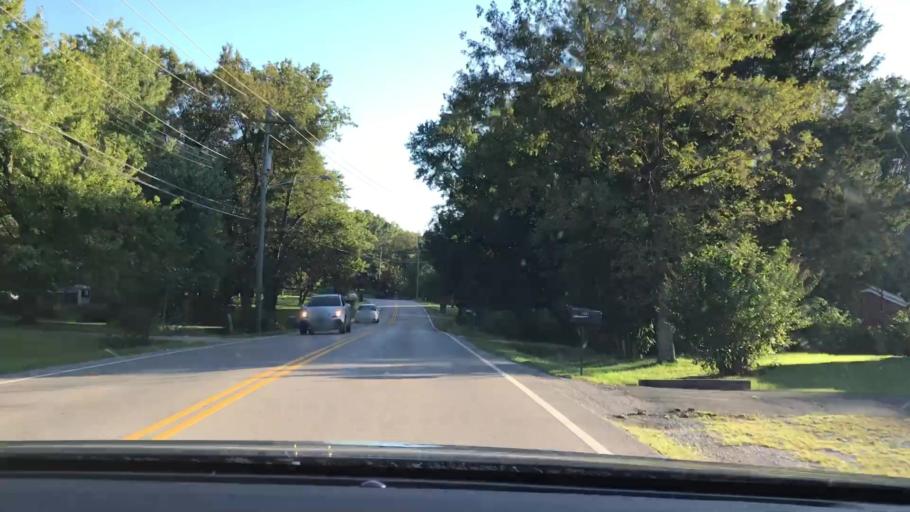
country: US
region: Tennessee
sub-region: Davidson County
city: Oak Hill
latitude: 36.0671
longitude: -86.6967
